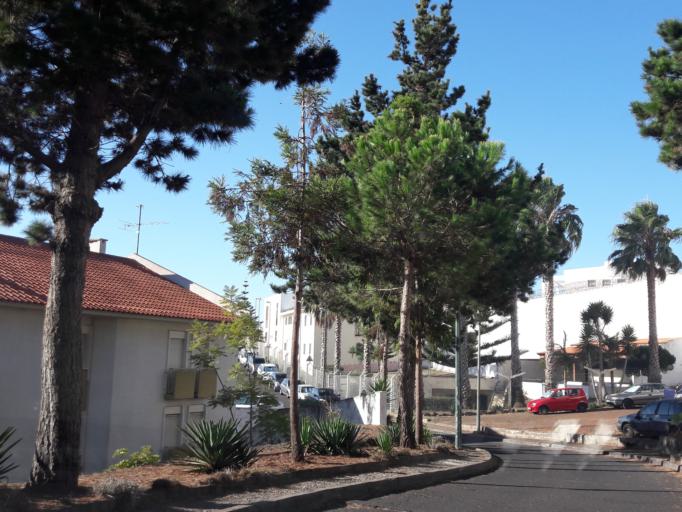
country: PT
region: Madeira
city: Canico
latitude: 32.6549
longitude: -16.8574
